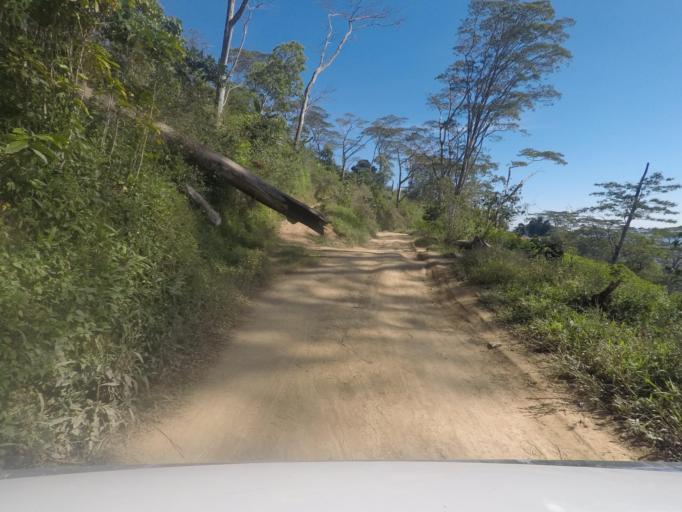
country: TL
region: Ermera
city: Gleno
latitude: -8.7370
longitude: 125.3442
